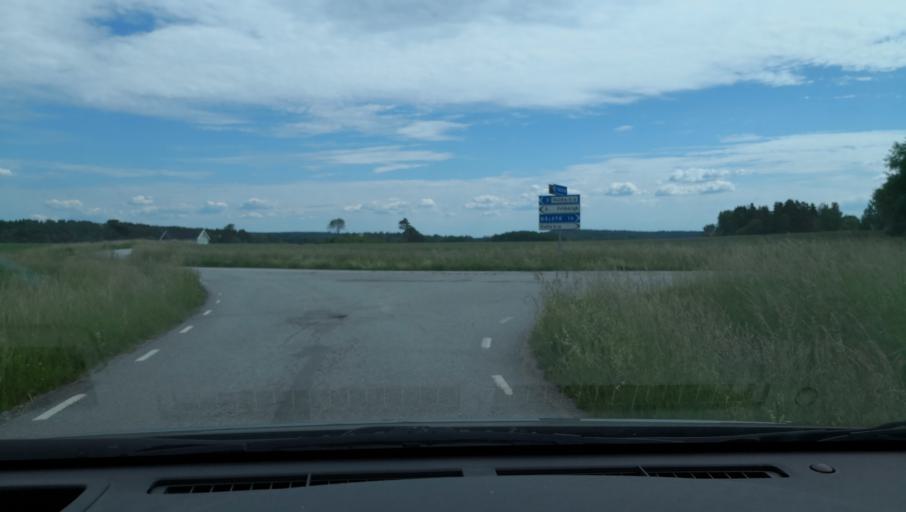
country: SE
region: Uppsala
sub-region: Habo Kommun
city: Balsta
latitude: 59.6930
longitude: 17.4708
